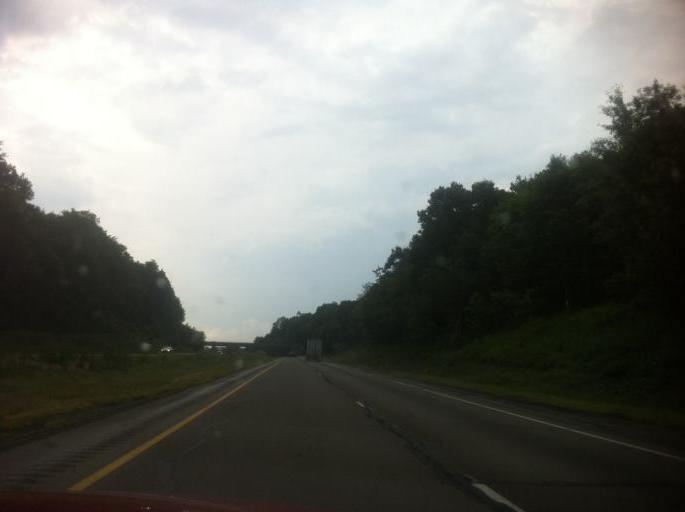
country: US
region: Pennsylvania
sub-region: Jefferson County
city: Brookville
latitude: 41.1671
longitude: -79.0092
